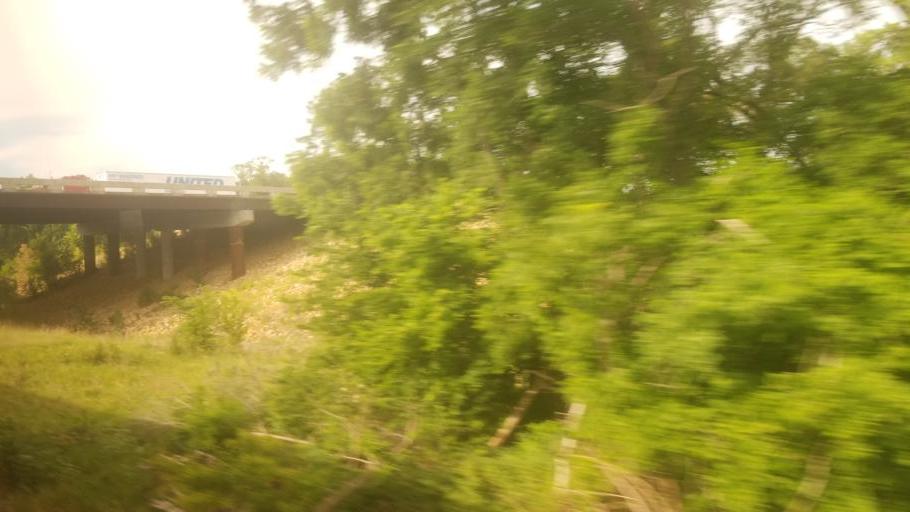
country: US
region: Kansas
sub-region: Douglas County
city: Lawrence
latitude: 38.9916
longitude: -95.2477
